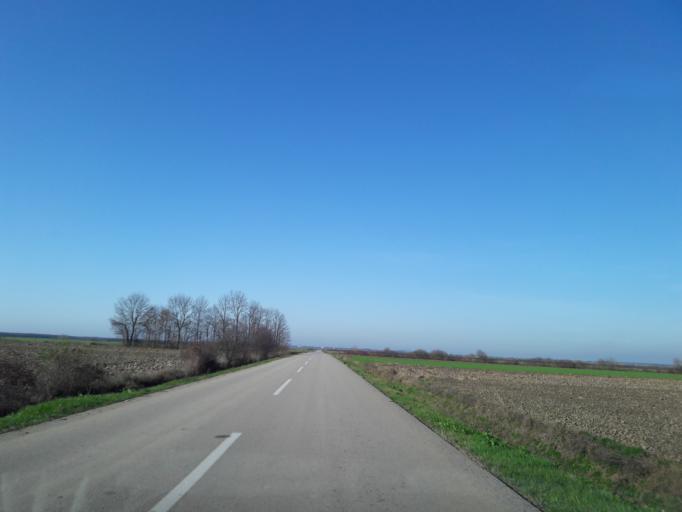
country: HR
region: Vukovarsko-Srijemska
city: Retkovci
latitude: 45.2419
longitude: 18.6427
